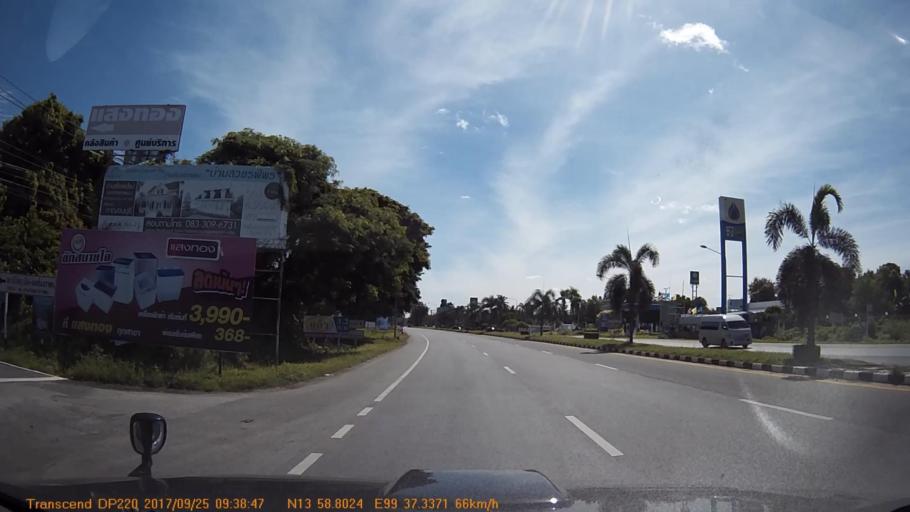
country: TH
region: Kanchanaburi
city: Tha Muang
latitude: 13.9801
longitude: 99.6225
